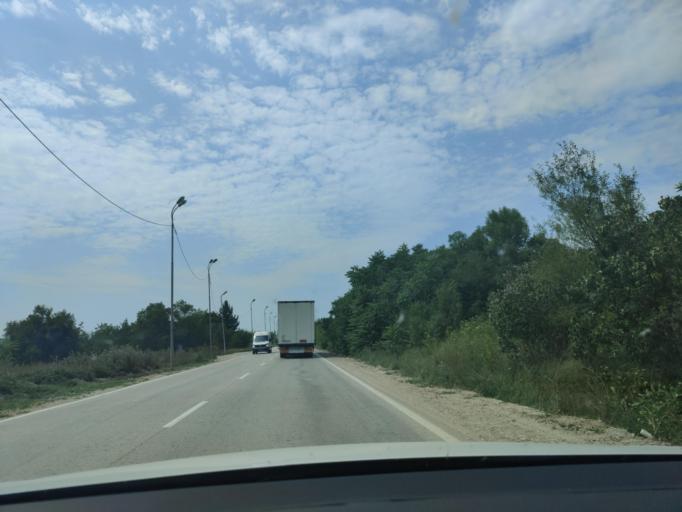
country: BG
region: Vidin
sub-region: Obshtina Dimovo
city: Dimovo
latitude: 43.7530
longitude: 22.7406
